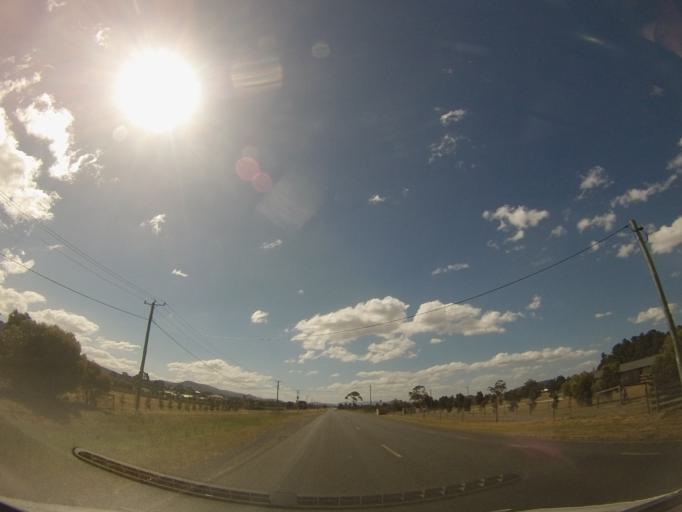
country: AU
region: Tasmania
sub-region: Clarence
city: Seven Mile Beach
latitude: -42.8589
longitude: 147.4919
